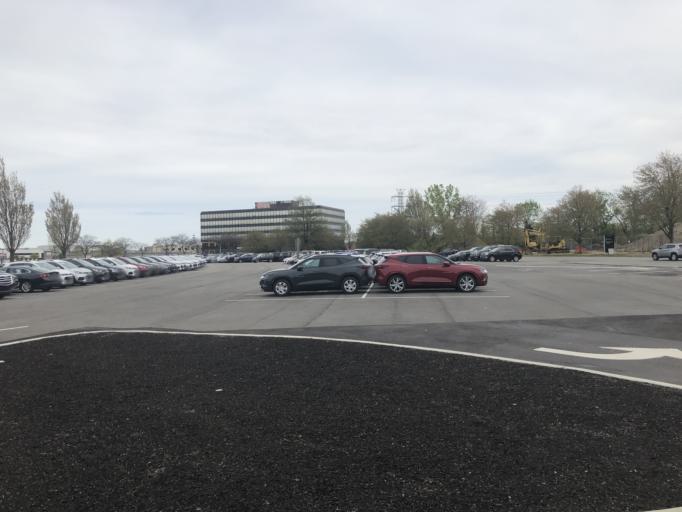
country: US
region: New York
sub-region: Nassau County
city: East Garden City
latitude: 40.7346
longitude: -73.6146
